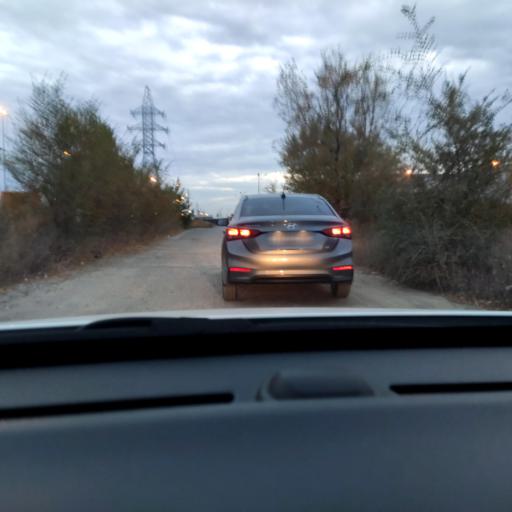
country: RU
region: Voronezj
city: Somovo
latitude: 51.6673
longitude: 39.2997
